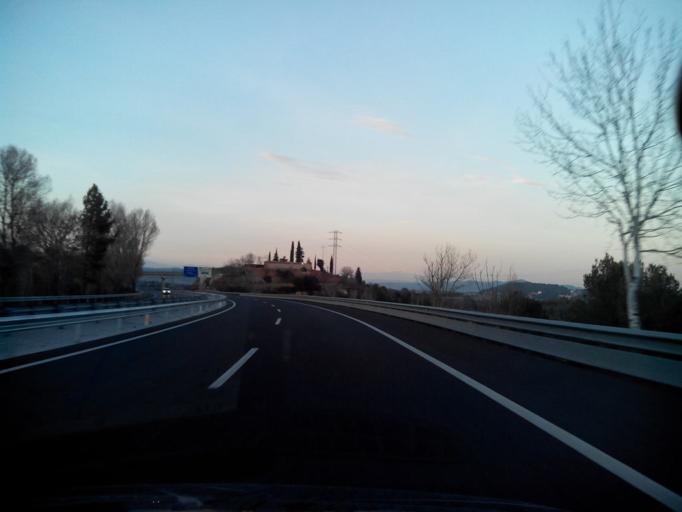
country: ES
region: Catalonia
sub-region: Provincia de Barcelona
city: Sant Fruitos de Bages
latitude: 41.7186
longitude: 1.8654
